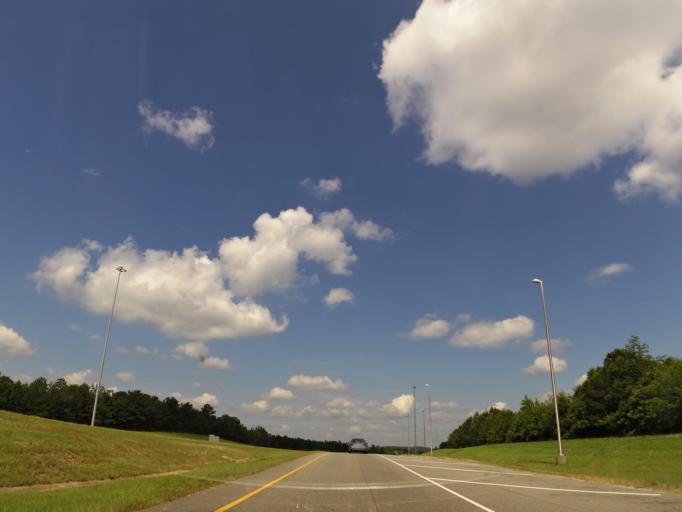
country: US
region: Alabama
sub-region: Marion County
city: Winfield
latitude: 33.9914
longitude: -87.7790
